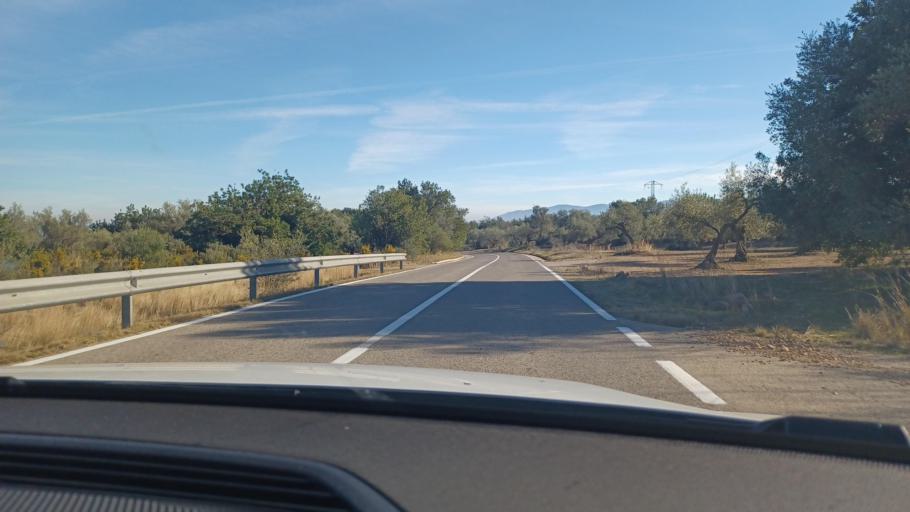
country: ES
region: Catalonia
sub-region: Provincia de Tarragona
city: Mas de Barberans
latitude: 40.7277
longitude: 0.3832
